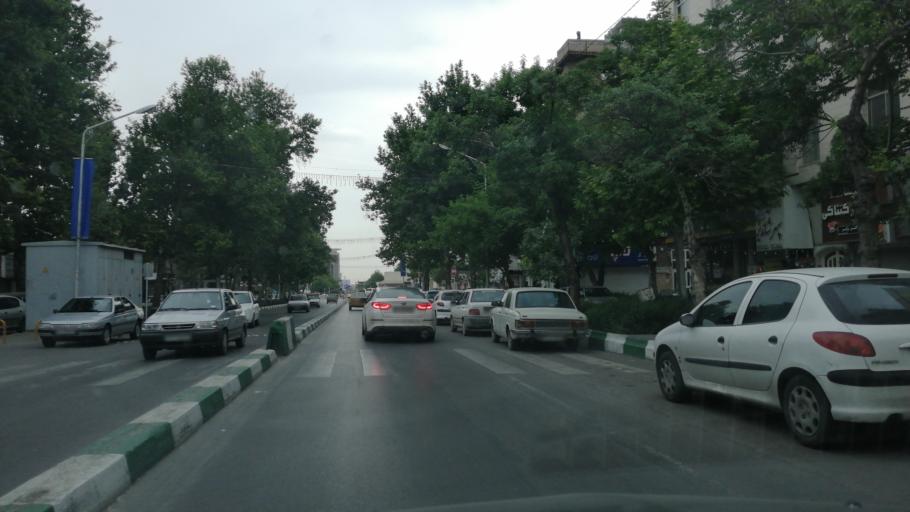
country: IR
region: Razavi Khorasan
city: Mashhad
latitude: 36.2900
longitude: 59.5828
